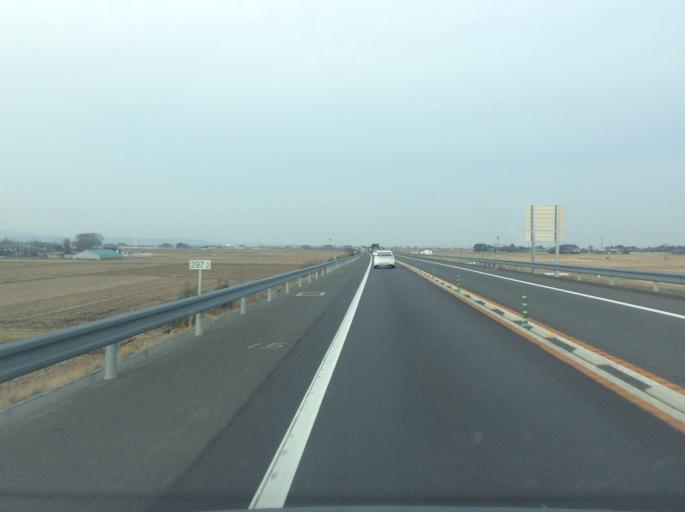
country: JP
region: Miyagi
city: Watari
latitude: 38.0570
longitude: 140.8937
